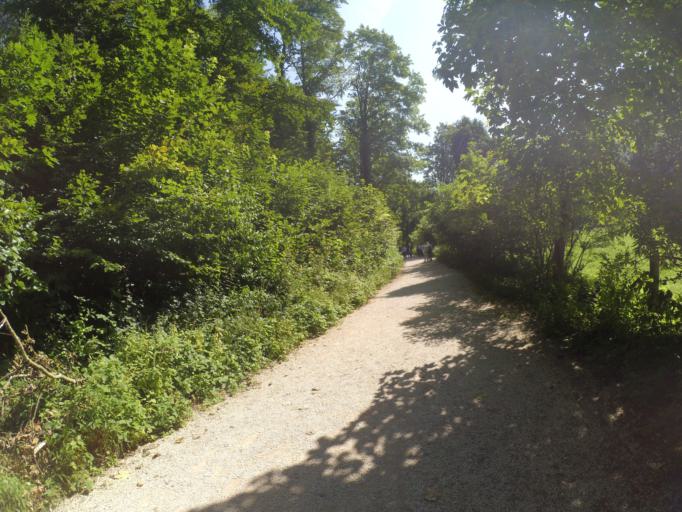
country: DE
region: Baden-Wuerttemberg
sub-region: Tuebingen Region
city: Bad Urach
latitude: 48.4936
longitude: 9.3719
